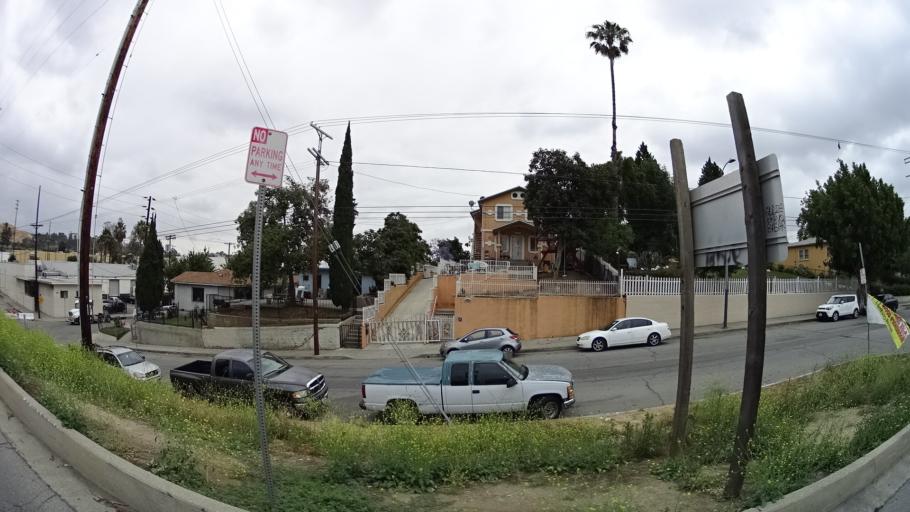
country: US
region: California
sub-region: Los Angeles County
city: Boyle Heights
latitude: 34.0633
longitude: -118.1976
